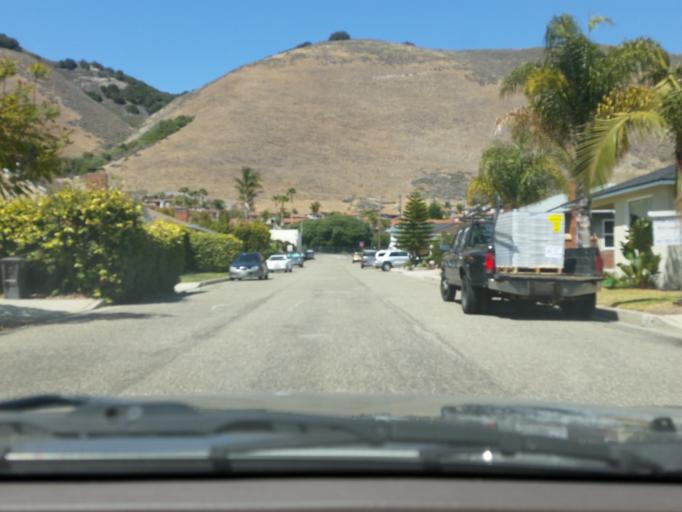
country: US
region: California
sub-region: San Luis Obispo County
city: Pismo Beach
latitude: 35.1561
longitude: -120.6724
